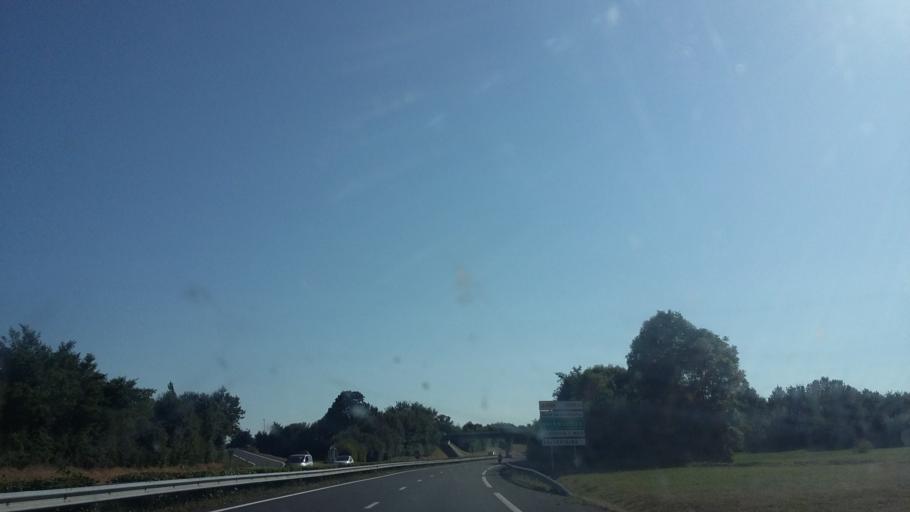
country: FR
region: Pays de la Loire
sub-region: Departement de la Vendee
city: Challans
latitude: 46.8594
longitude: -1.8789
